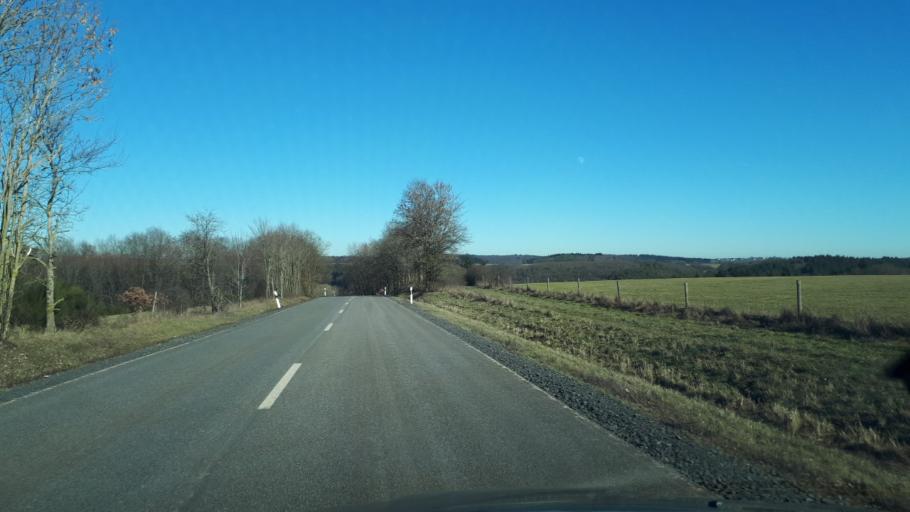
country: DE
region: Rheinland-Pfalz
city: Oberscheidweiler
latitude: 50.0791
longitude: 6.9419
